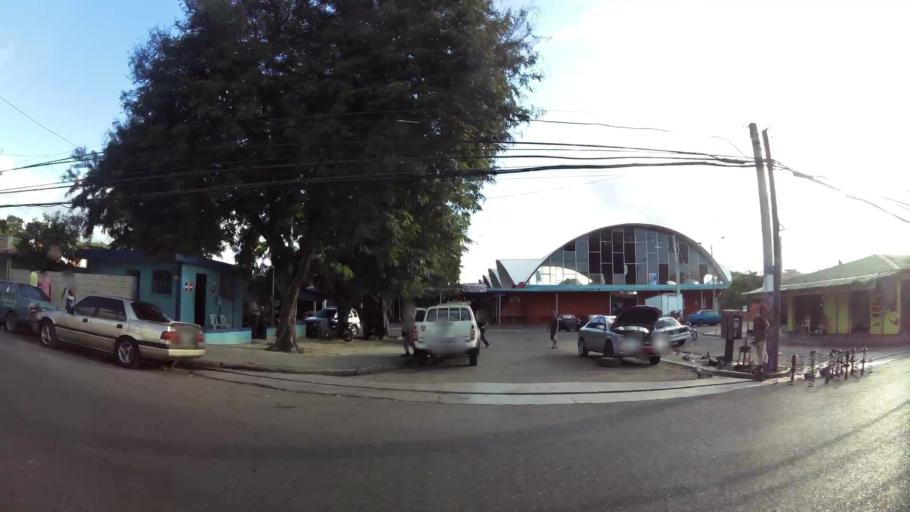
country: DO
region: Santiago
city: Santiago de los Caballeros
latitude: 19.4613
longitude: -70.7040
